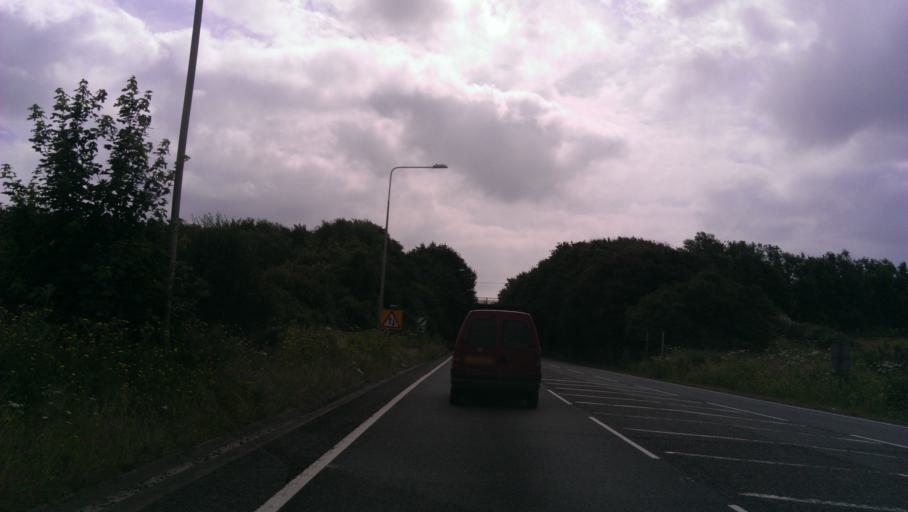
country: GB
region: England
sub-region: Kent
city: Dover
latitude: 51.1512
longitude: 1.3177
